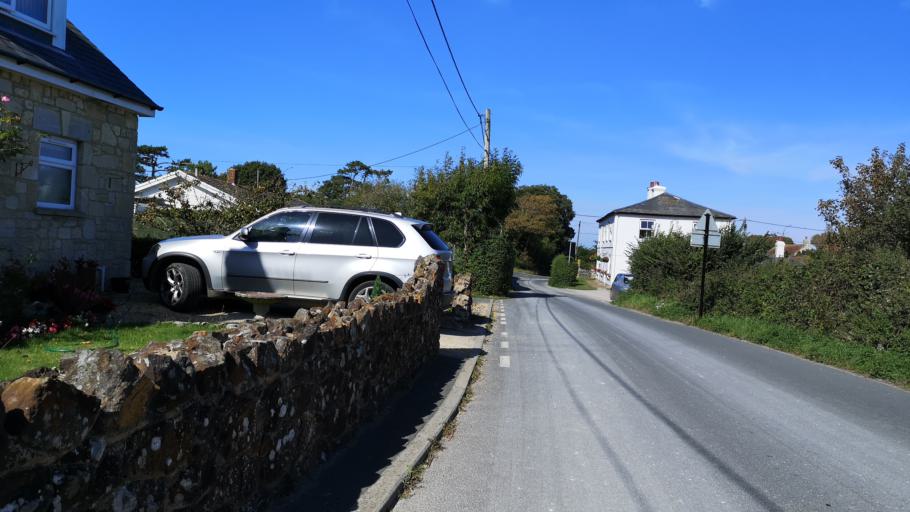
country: GB
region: England
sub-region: Isle of Wight
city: Totland
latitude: 50.6712
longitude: -1.5426
